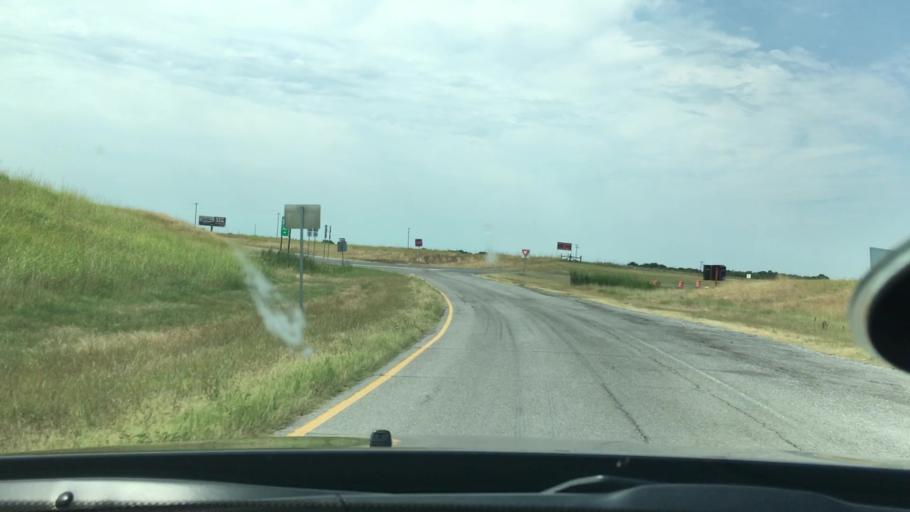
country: US
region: Oklahoma
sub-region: Carter County
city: Ardmore
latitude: 34.3336
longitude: -97.1532
